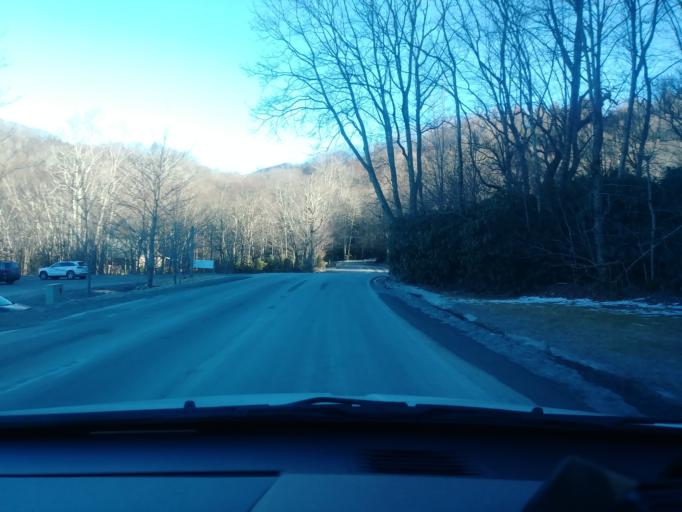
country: US
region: North Carolina
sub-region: Avery County
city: Banner Elk
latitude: 36.1291
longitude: -81.8551
